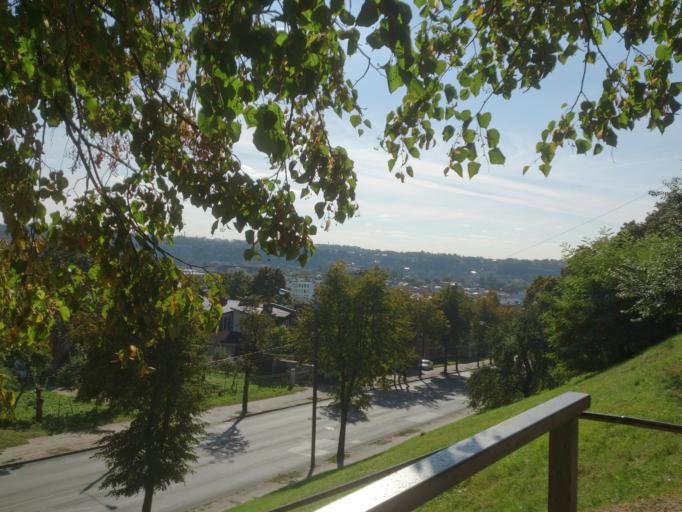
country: LT
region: Kauno apskritis
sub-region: Kaunas
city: Kaunas
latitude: 54.9021
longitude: 23.9095
